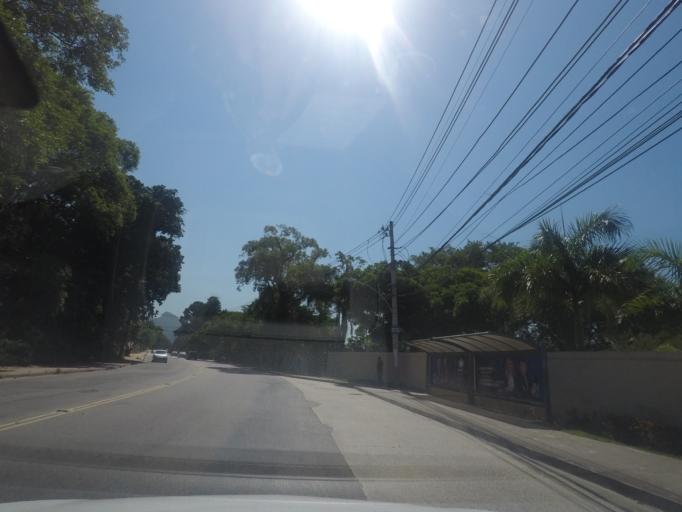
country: BR
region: Rio de Janeiro
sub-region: Nilopolis
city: Nilopolis
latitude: -22.9881
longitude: -43.4823
